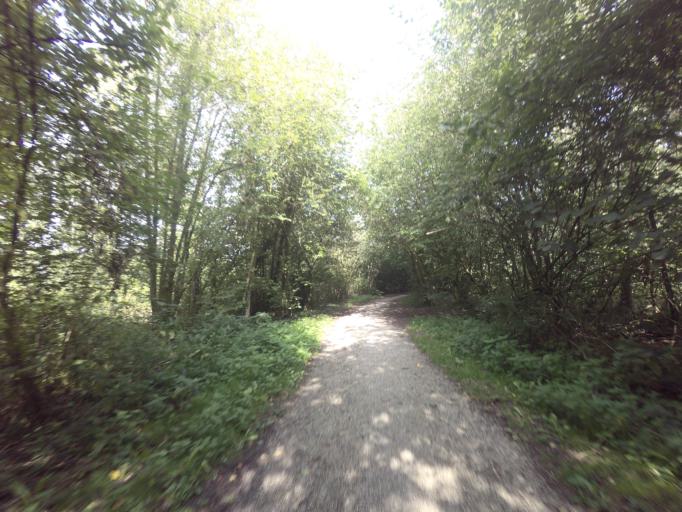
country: NL
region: Groningen
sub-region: Gemeente Zuidhorn
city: Grijpskerk
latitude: 53.2163
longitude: 6.3371
